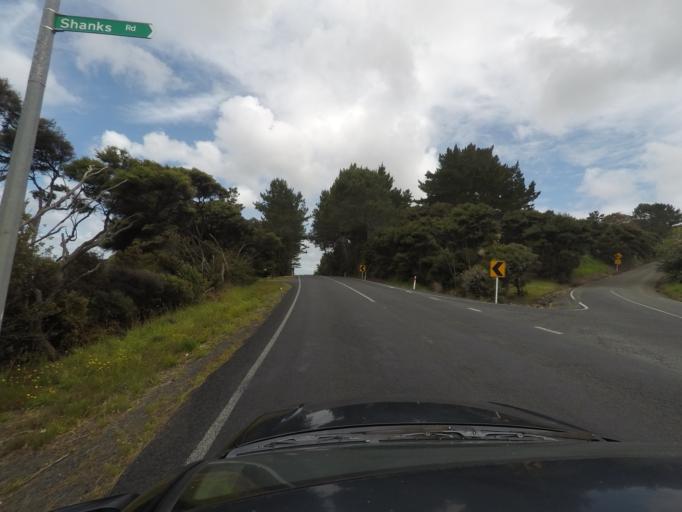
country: NZ
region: Auckland
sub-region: Auckland
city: Parakai
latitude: -36.6377
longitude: 174.5063
